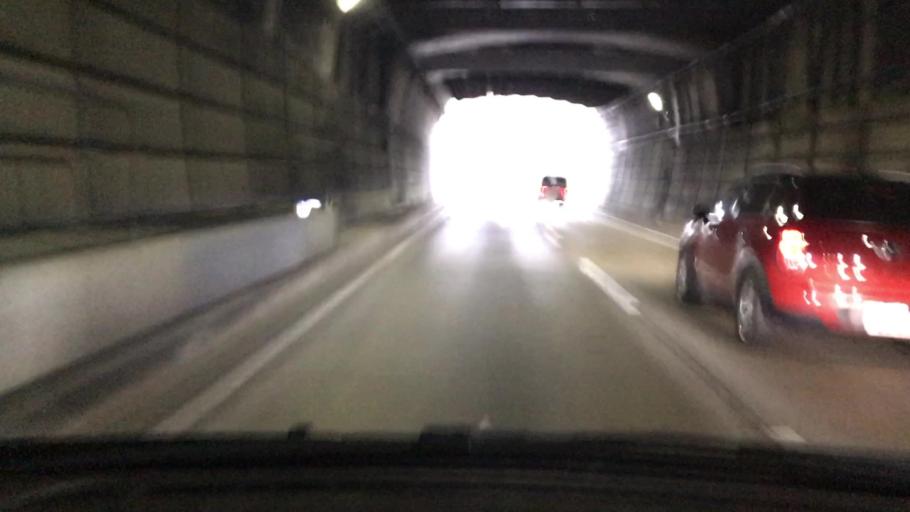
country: JP
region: Hyogo
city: Kobe
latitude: 34.7635
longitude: 135.1529
